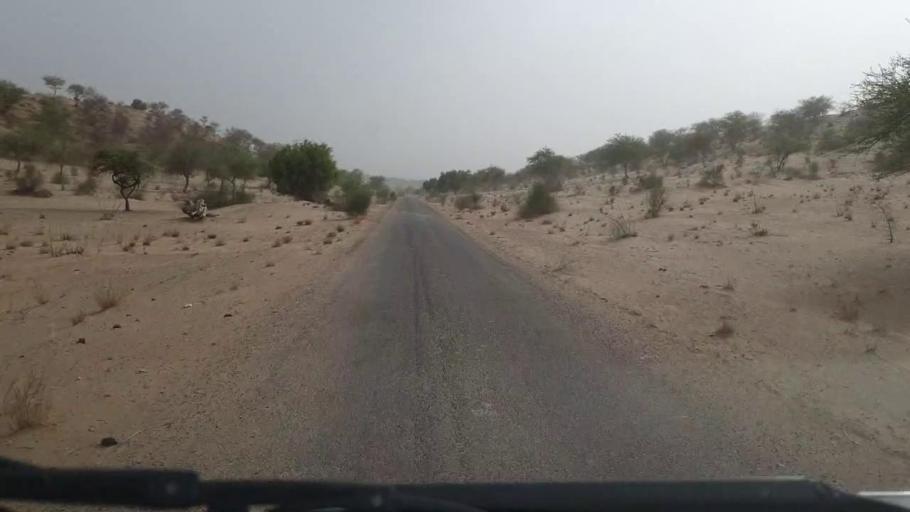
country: PK
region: Sindh
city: Islamkot
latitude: 25.0602
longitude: 70.5343
